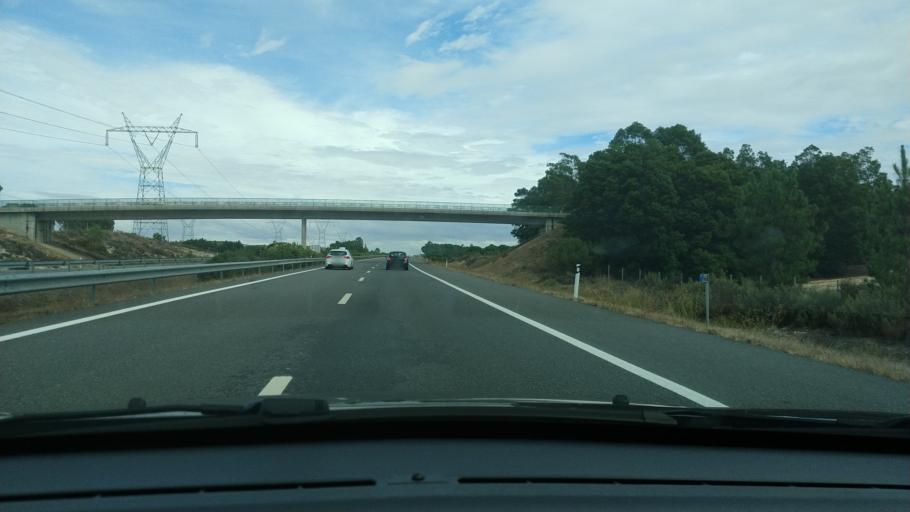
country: PT
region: Setubal
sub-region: Grandola
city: Grandola
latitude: 38.2536
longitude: -8.5218
